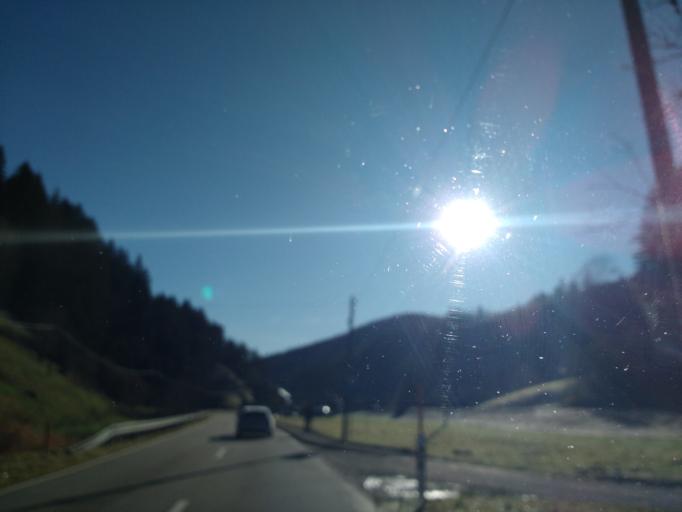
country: DE
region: Baden-Wuerttemberg
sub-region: Karlsruhe Region
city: Bad Rippoldsau-Schapbach
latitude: 48.4418
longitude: 8.3137
